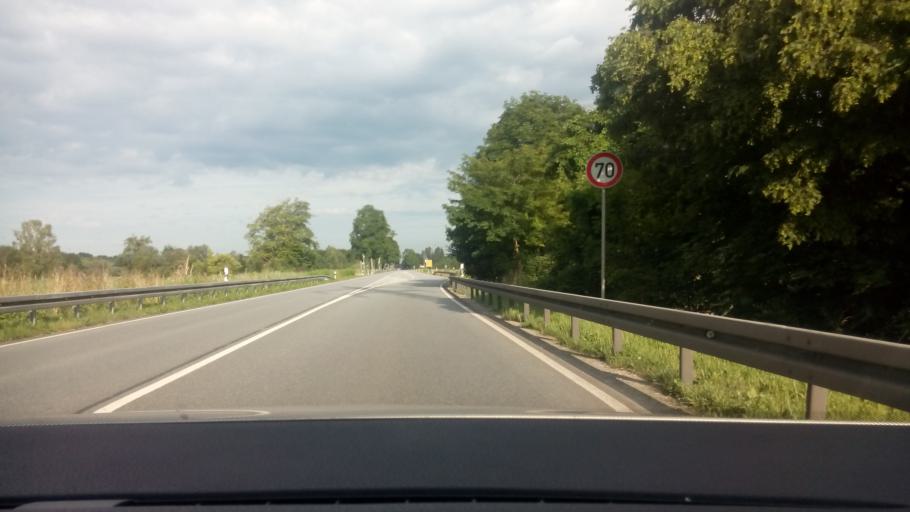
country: DE
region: Bavaria
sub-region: Upper Bavaria
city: Oberschleissheim
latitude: 48.2530
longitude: 11.5202
